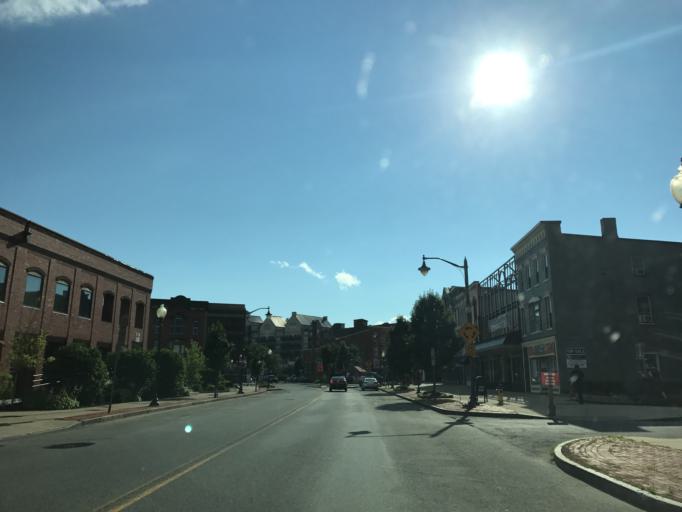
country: US
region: New York
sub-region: Warren County
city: Glens Falls
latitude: 43.3097
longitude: -73.6426
